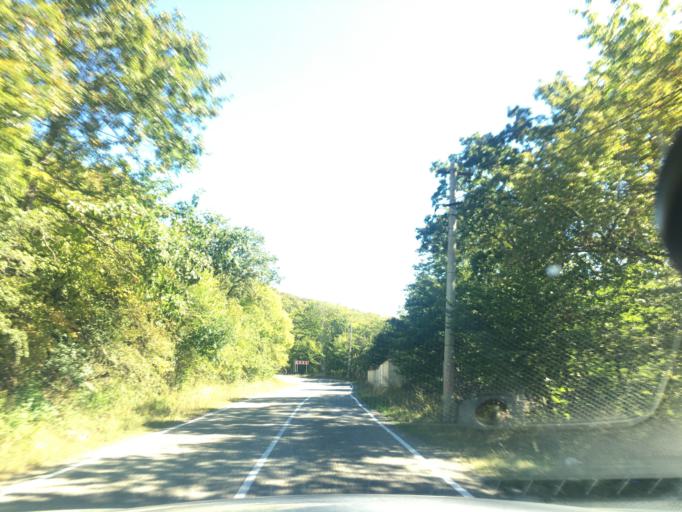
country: GE
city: Didi Lilo
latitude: 41.8869
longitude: 44.9212
